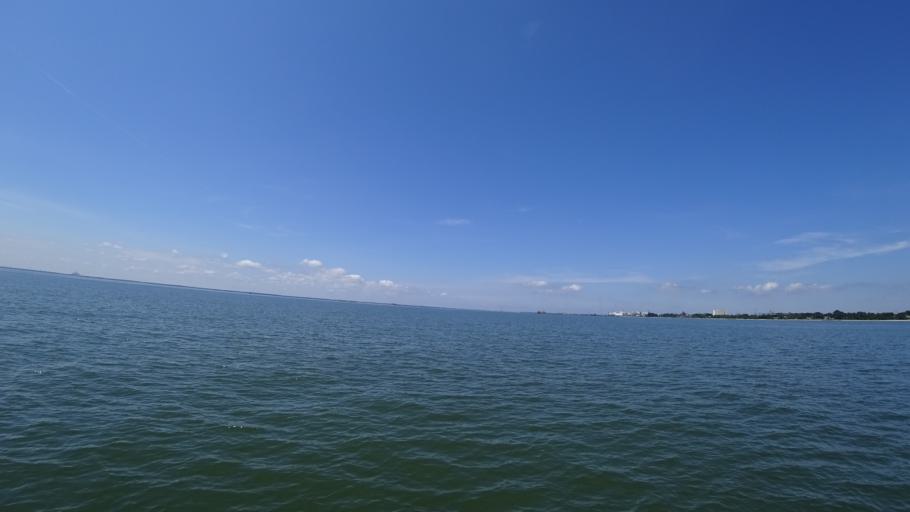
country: US
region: Virginia
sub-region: City of Newport News
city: Newport News
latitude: 36.9751
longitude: -76.3887
